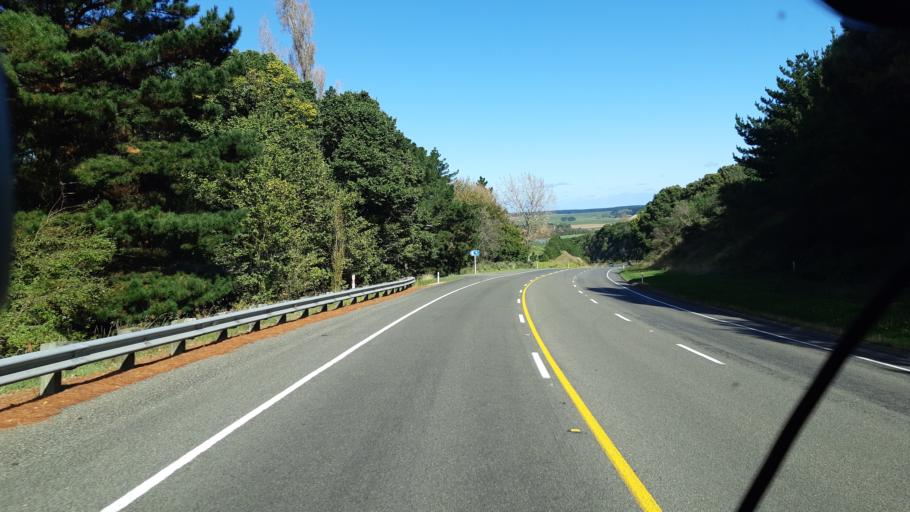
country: NZ
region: Manawatu-Wanganui
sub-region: Wanganui District
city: Wanganui
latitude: -39.9971
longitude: 175.1692
